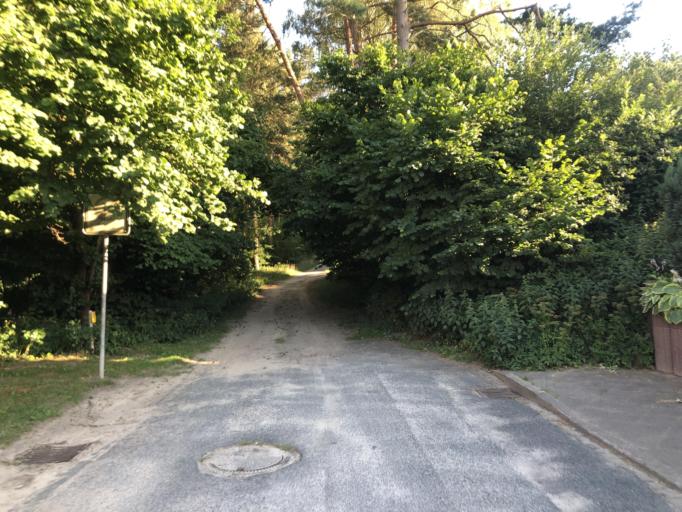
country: DE
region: Lower Saxony
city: Tosterglope
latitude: 53.2601
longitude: 10.7915
